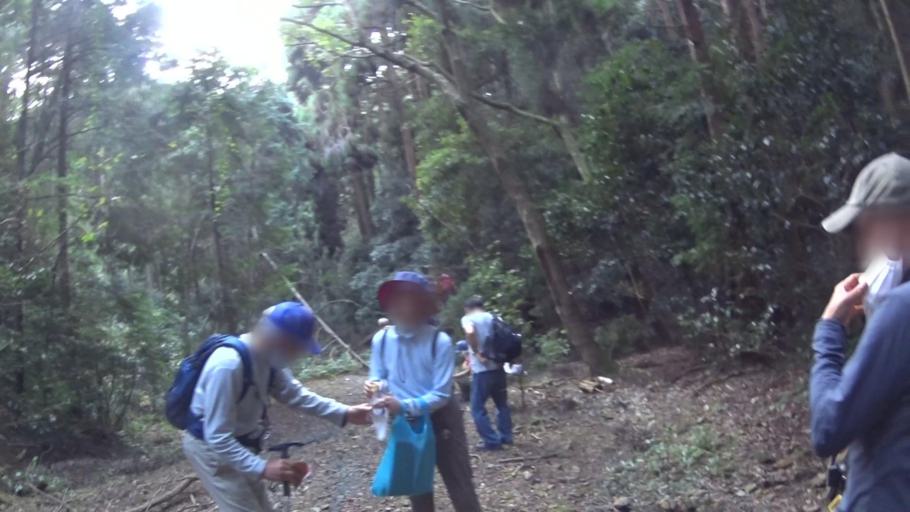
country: JP
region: Osaka
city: Kaizuka
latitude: 34.4809
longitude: 135.3135
